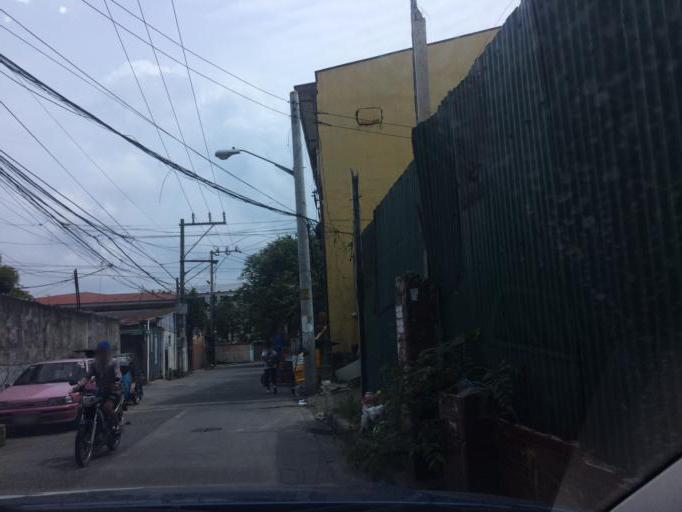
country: PH
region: Metro Manila
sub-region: Makati City
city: Makati City
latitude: 14.5448
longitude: 121.0064
